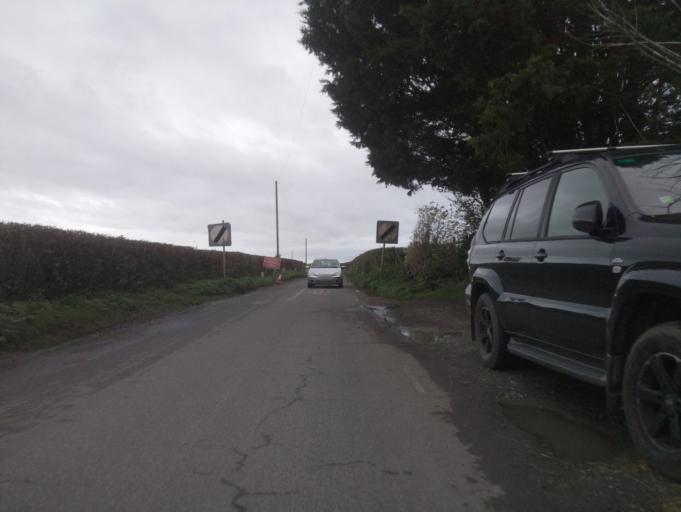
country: GB
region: England
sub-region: Somerset
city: Yeovil
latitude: 51.0011
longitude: -2.5871
